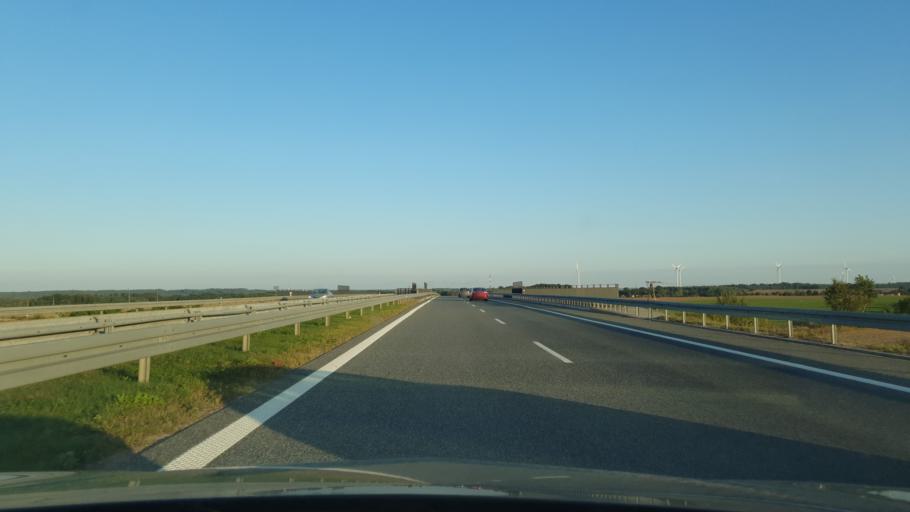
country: PL
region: Pomeranian Voivodeship
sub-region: Powiat slupski
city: Kobylnica
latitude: 54.4385
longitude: 16.9532
